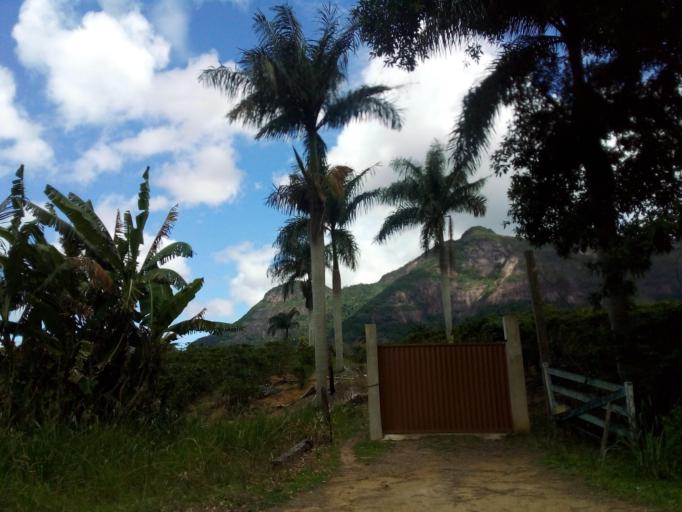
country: BR
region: Espirito Santo
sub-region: Ibiracu
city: Ibiracu
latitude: -19.8886
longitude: -40.3644
